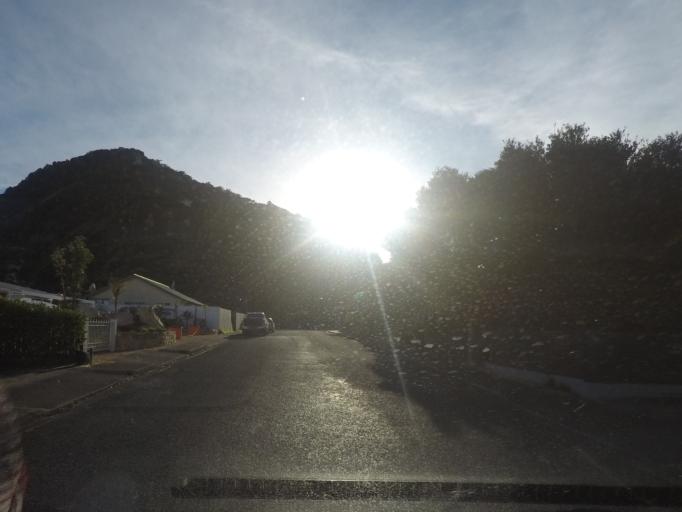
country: NZ
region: Tasman
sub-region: Tasman District
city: Takaka
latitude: -40.8099
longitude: 172.9170
